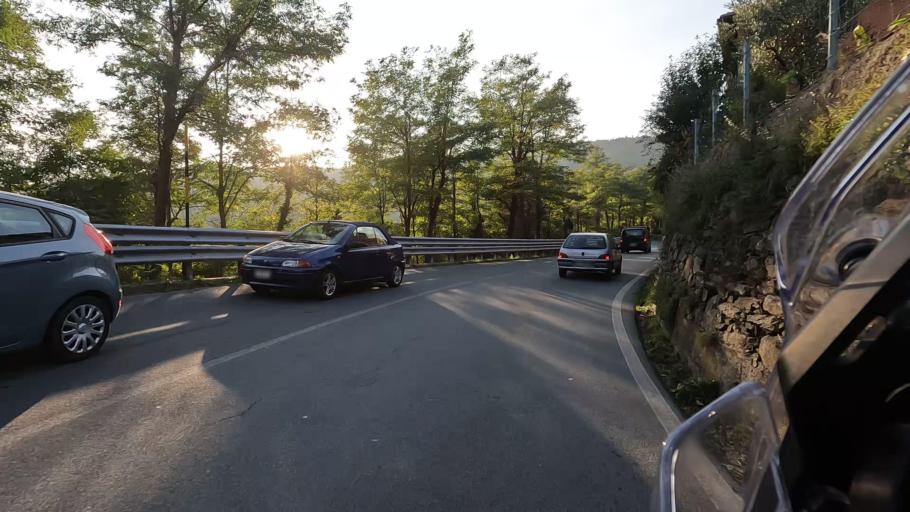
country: IT
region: Liguria
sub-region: Provincia di Savona
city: San Giovanni
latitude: 44.4082
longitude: 8.4880
